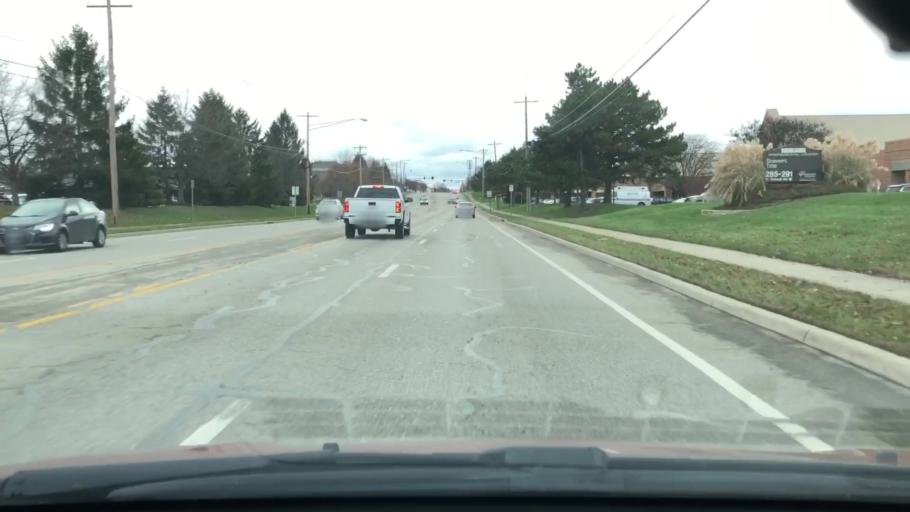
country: US
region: Ohio
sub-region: Franklin County
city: Westerville
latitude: 40.1101
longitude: -82.9351
